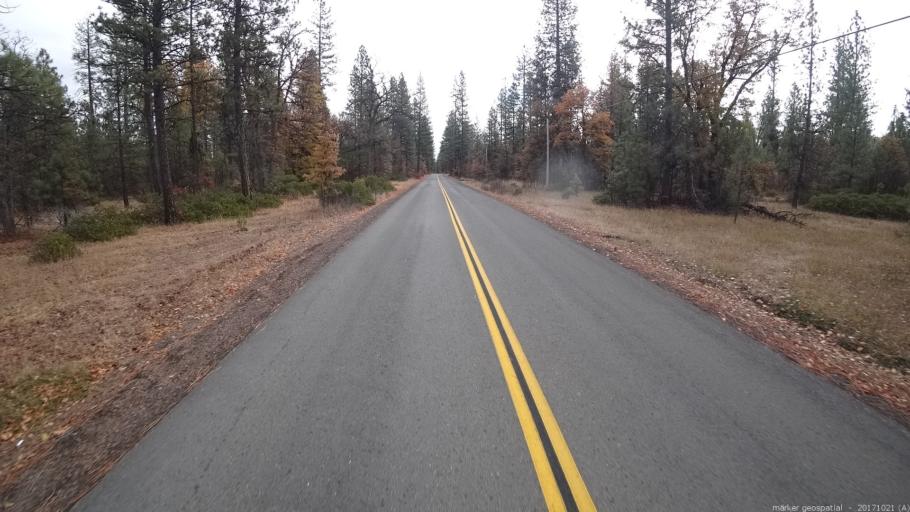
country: US
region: California
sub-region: Shasta County
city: Burney
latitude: 41.0039
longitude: -121.6427
